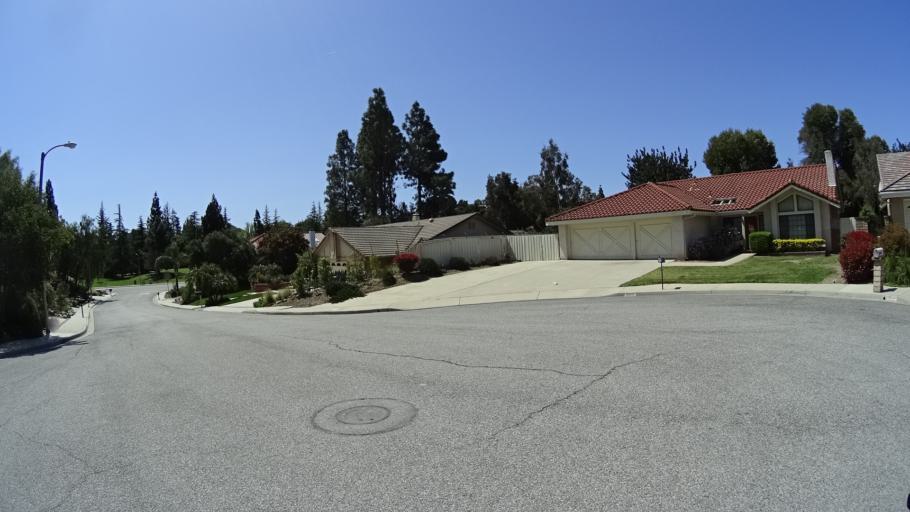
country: US
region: California
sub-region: Ventura County
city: Casa Conejo
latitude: 34.2068
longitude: -118.8905
